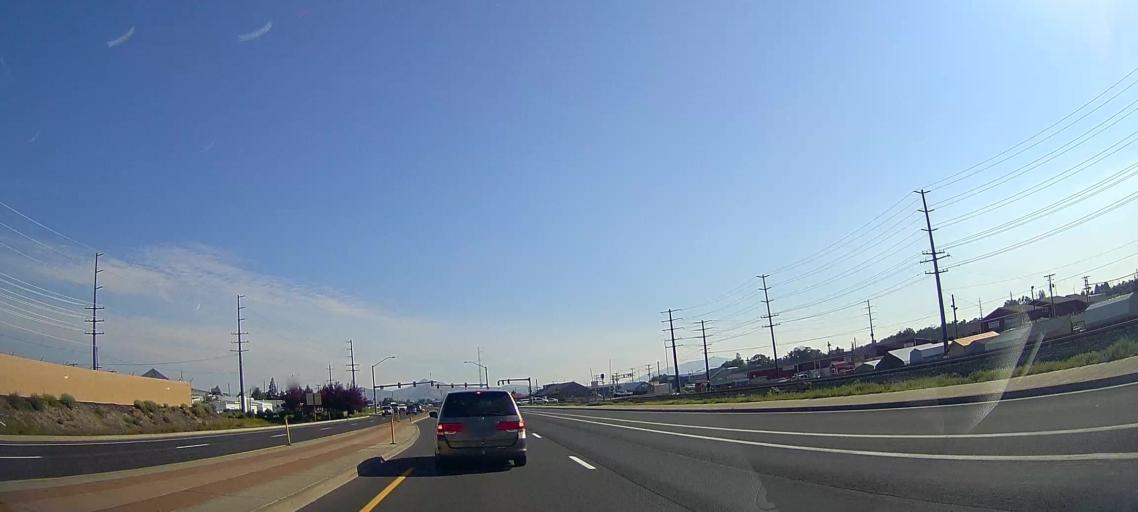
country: US
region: Oregon
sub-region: Deschutes County
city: Redmond
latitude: 44.2710
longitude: -121.1704
